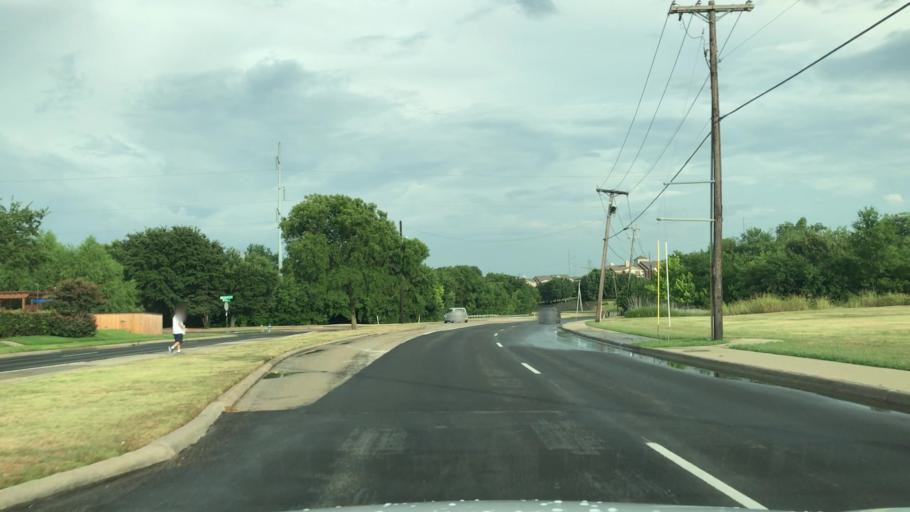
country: US
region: Texas
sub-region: Dallas County
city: Garland
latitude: 32.8403
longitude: -96.6232
